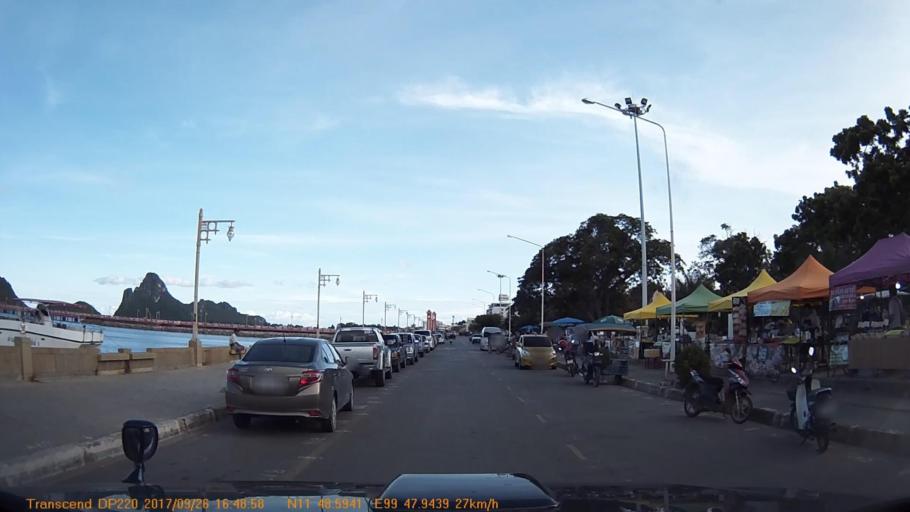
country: TH
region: Prachuap Khiri Khan
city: Prachuap Khiri Khan
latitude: 11.8099
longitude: 99.7991
